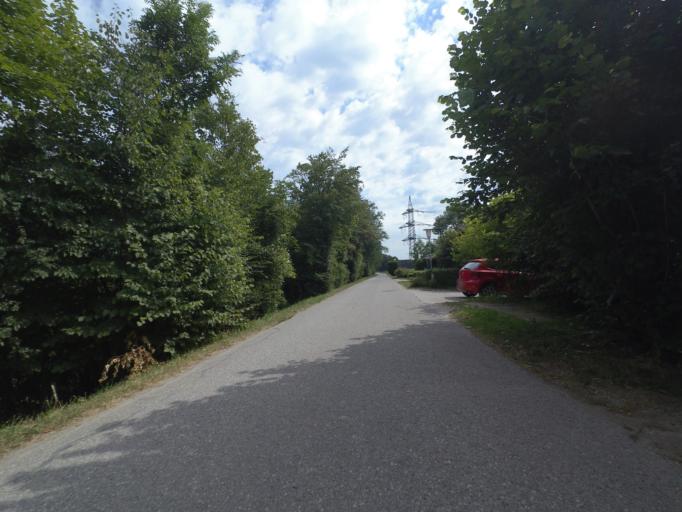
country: DE
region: Bavaria
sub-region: Upper Bavaria
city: Ainring
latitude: 47.7946
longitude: 12.9574
